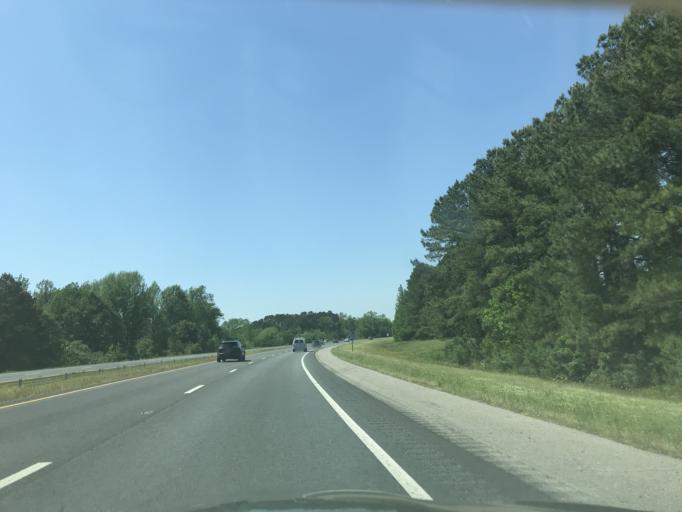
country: US
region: North Carolina
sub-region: Johnston County
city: Benson
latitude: 35.3325
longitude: -78.4569
